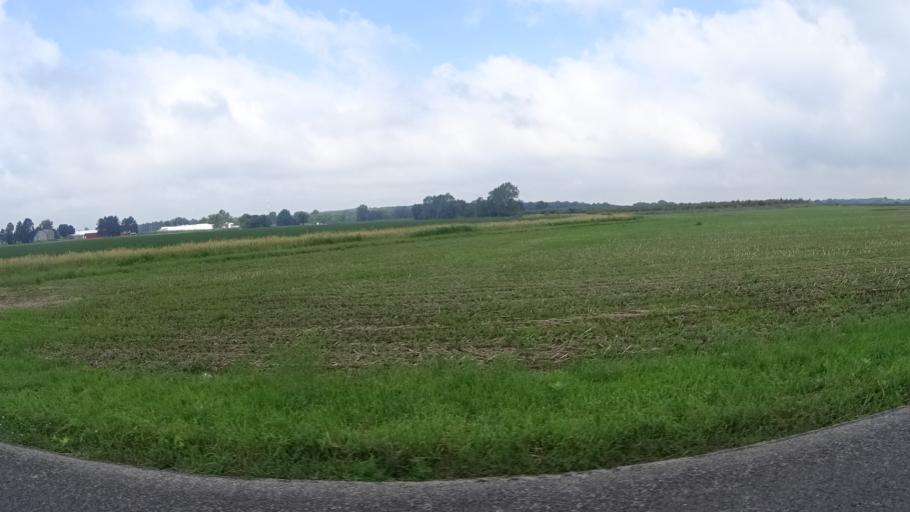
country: US
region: Ohio
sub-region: Huron County
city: Wakeman
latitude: 41.3097
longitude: -82.4660
